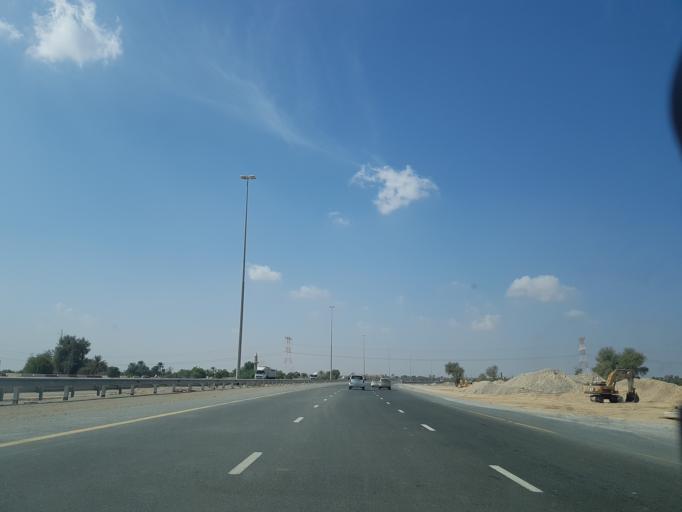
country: AE
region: Ra's al Khaymah
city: Ras al-Khaimah
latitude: 25.6988
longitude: 55.9869
